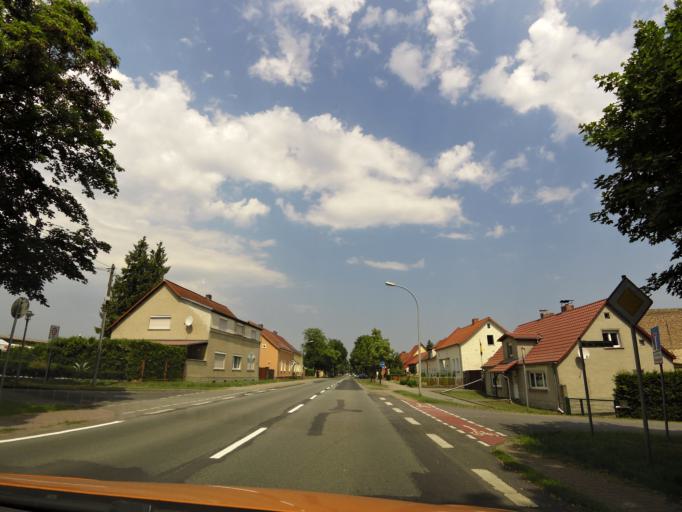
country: DE
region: Brandenburg
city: Wustermark
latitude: 52.4922
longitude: 12.9265
